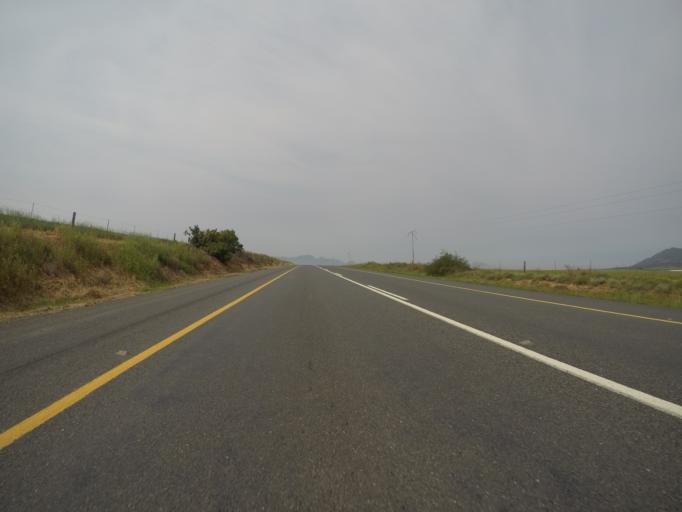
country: ZA
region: Western Cape
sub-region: West Coast District Municipality
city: Malmesbury
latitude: -33.5501
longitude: 18.8683
